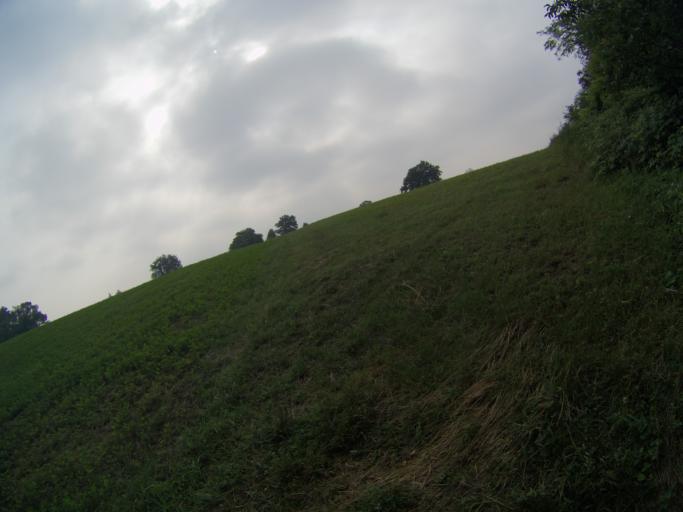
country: IT
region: Emilia-Romagna
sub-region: Provincia di Reggio Emilia
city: Albinea
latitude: 44.6311
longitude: 10.6185
